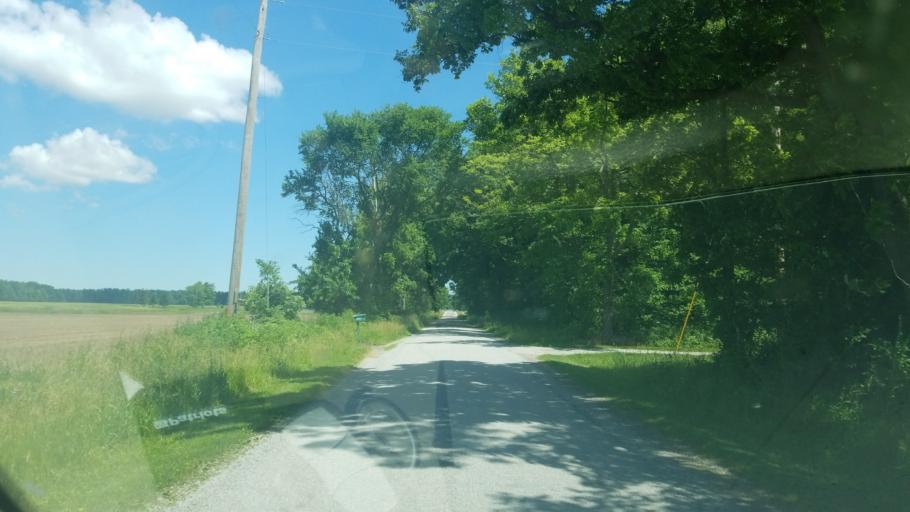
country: US
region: Ohio
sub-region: Huron County
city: New London
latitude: 41.1575
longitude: -82.3897
